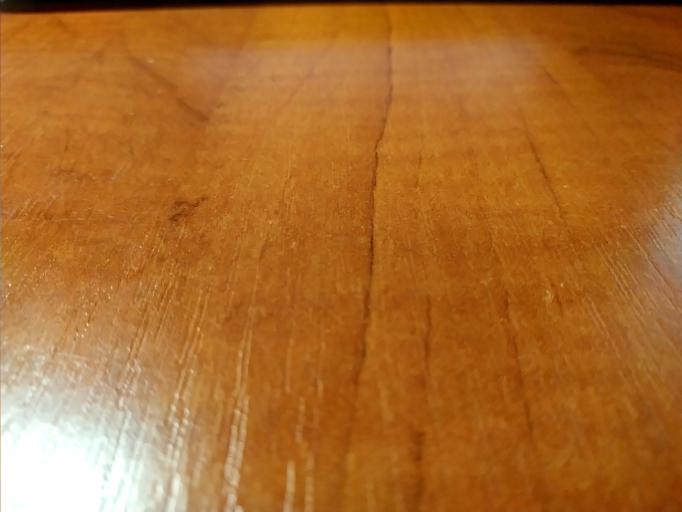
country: RU
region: Vologda
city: Khokhlovo
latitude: 59.3480
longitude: 37.3640
